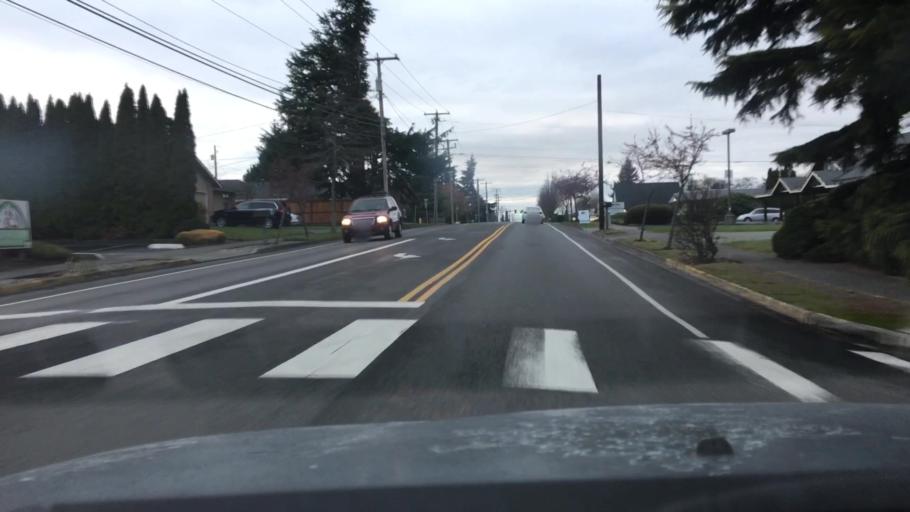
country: US
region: Washington
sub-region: Skagit County
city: Mount Vernon
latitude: 48.4210
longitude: -122.3190
